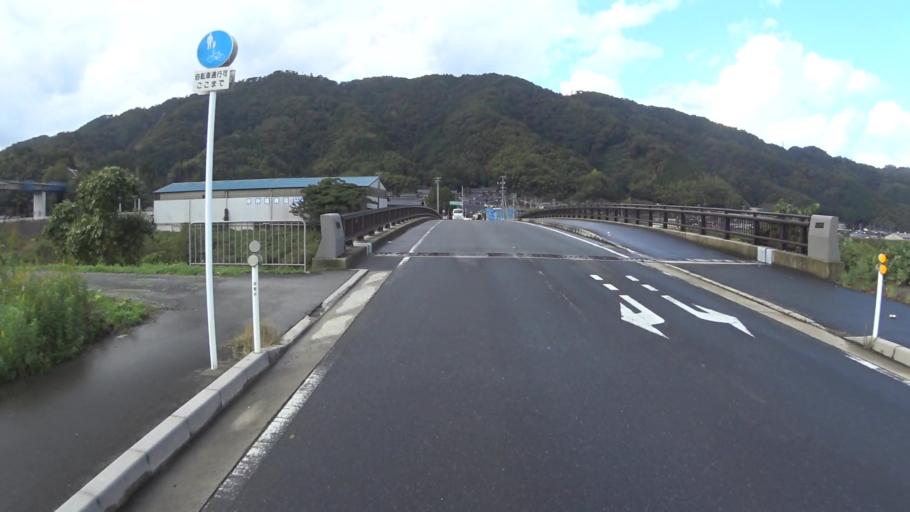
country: JP
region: Kyoto
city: Miyazu
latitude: 35.5524
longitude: 135.1407
